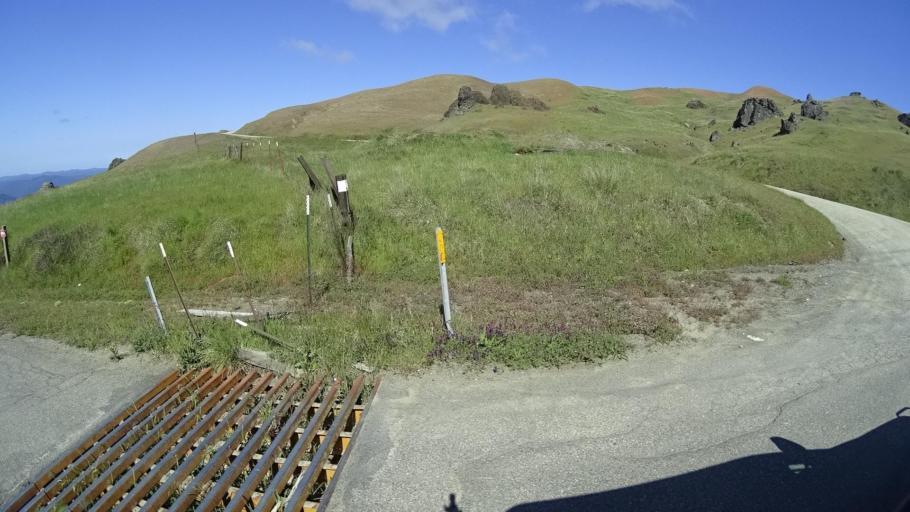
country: US
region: California
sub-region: Humboldt County
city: Redway
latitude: 40.1074
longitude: -123.6997
